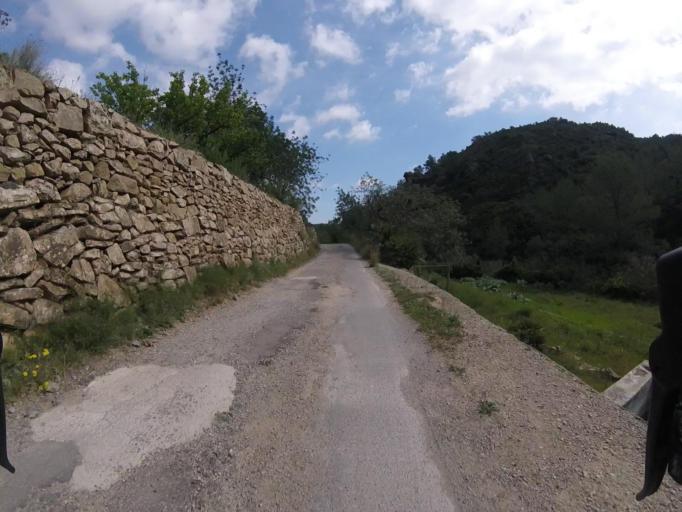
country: ES
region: Valencia
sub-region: Provincia de Castello
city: Cabanes
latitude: 40.1093
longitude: 0.0426
